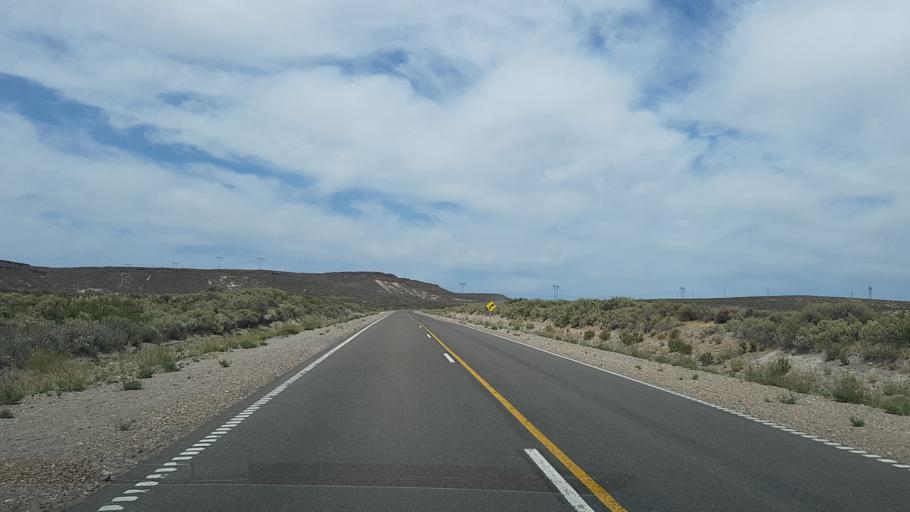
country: AR
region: Neuquen
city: Piedra del Aguila
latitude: -39.9704
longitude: -70.0178
